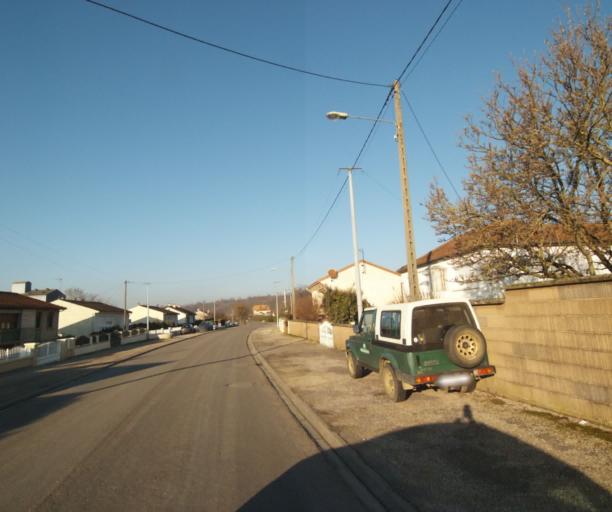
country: FR
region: Champagne-Ardenne
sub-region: Departement de la Haute-Marne
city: Bienville
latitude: 48.5767
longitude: 5.0456
